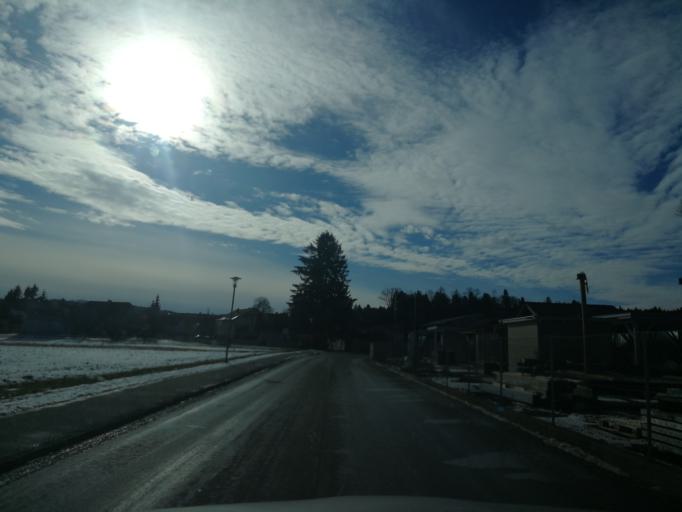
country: AT
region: Styria
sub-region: Politischer Bezirk Weiz
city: Ungerdorf
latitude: 47.1021
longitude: 15.6710
